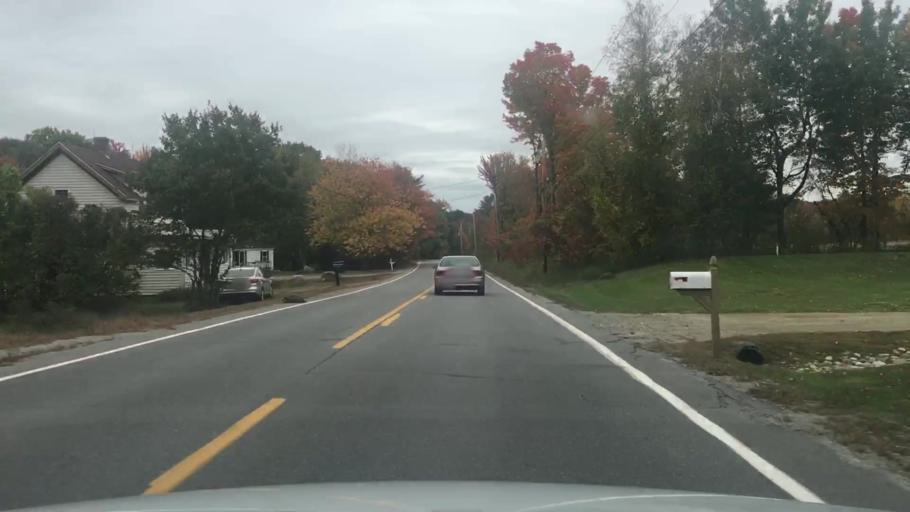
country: US
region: Maine
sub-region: Kennebec County
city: Oakland
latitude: 44.5434
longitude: -69.7946
